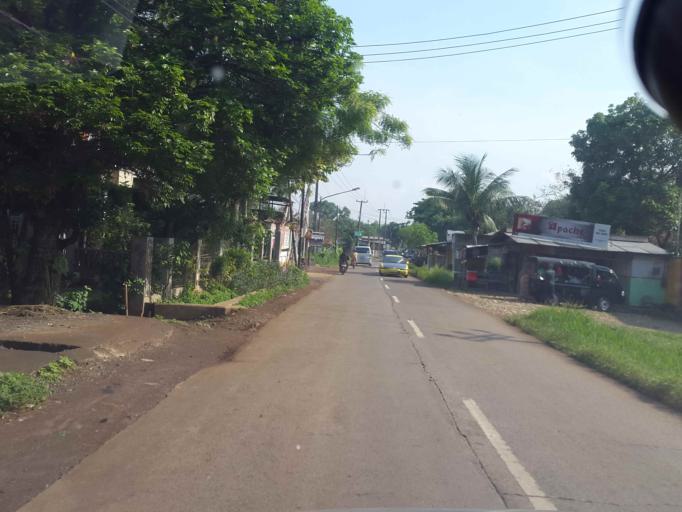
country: ID
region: West Java
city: Cileungsir
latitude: -6.3459
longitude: 107.0354
